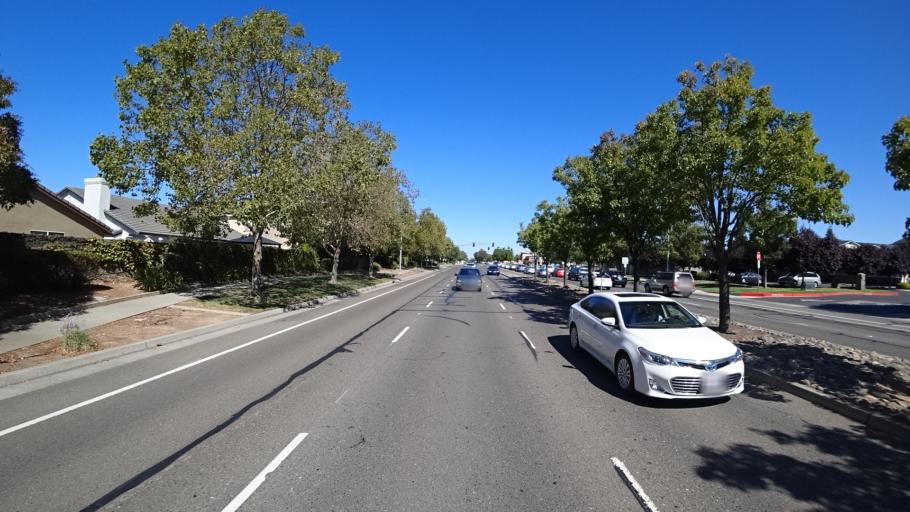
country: US
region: California
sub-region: Sacramento County
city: Vineyard
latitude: 38.4478
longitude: -121.3718
